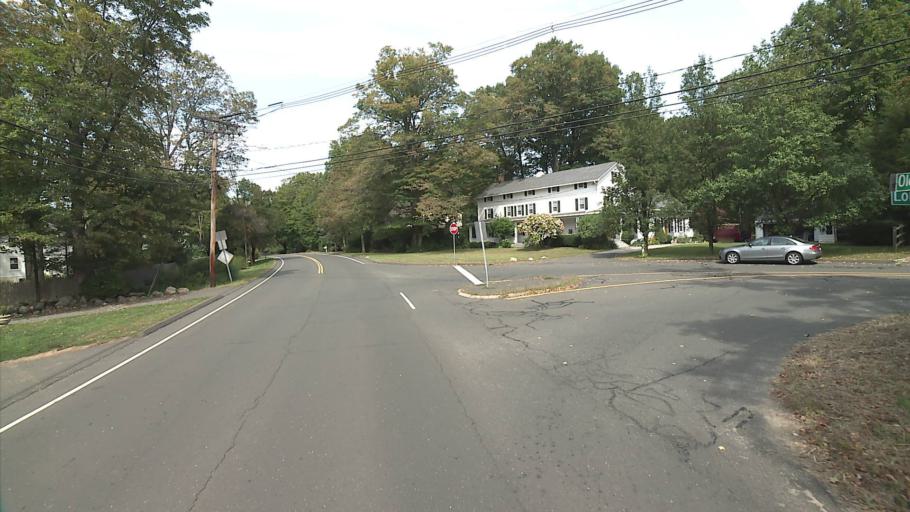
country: US
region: New York
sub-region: Westchester County
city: Pound Ridge
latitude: 41.1584
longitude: -73.5962
